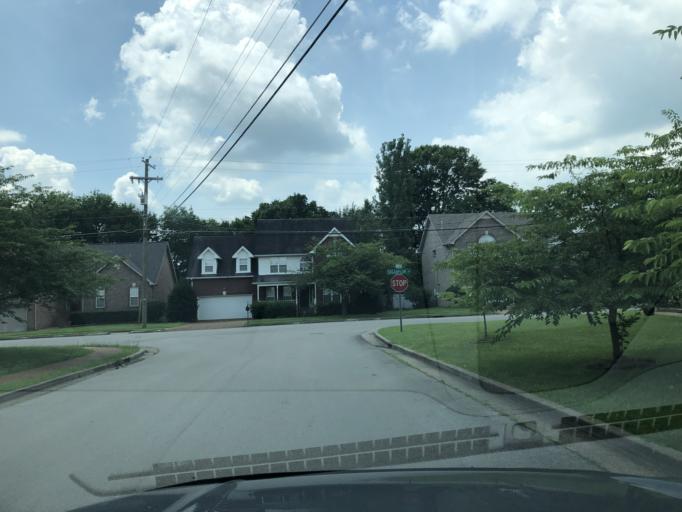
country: US
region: Tennessee
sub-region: Williamson County
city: Nolensville
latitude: 36.0132
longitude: -86.6943
